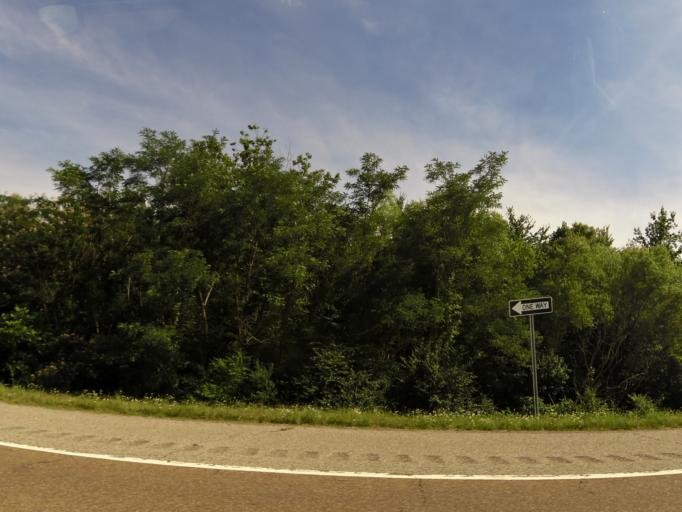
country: US
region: Tennessee
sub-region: Carroll County
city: Huntingdon
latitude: 36.0249
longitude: -88.4106
